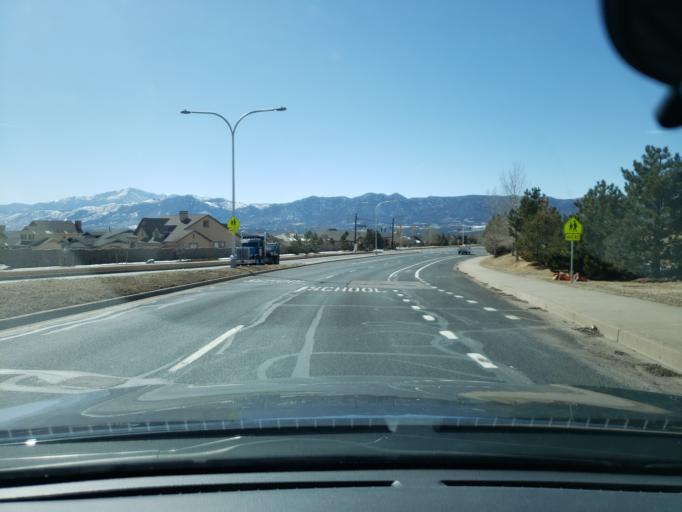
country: US
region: Colorado
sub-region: El Paso County
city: Gleneagle
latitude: 39.0277
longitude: -104.7974
